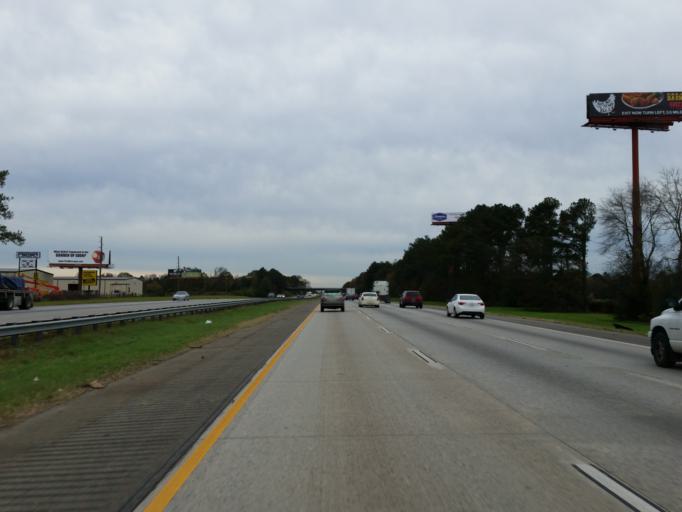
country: US
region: Georgia
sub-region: Peach County
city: Byron
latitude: 32.6487
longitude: -83.7440
